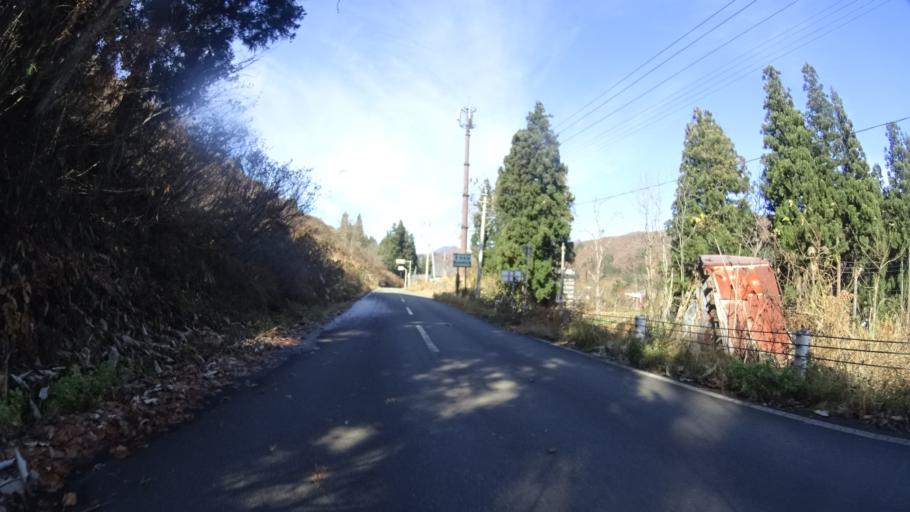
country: JP
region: Niigata
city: Muikamachi
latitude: 37.1900
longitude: 139.0814
